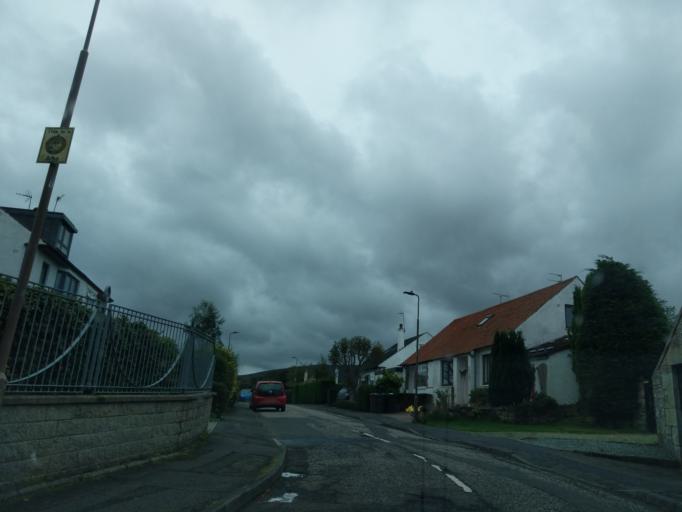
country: GB
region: Scotland
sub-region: Edinburgh
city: Balerno
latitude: 55.8827
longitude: -3.3452
